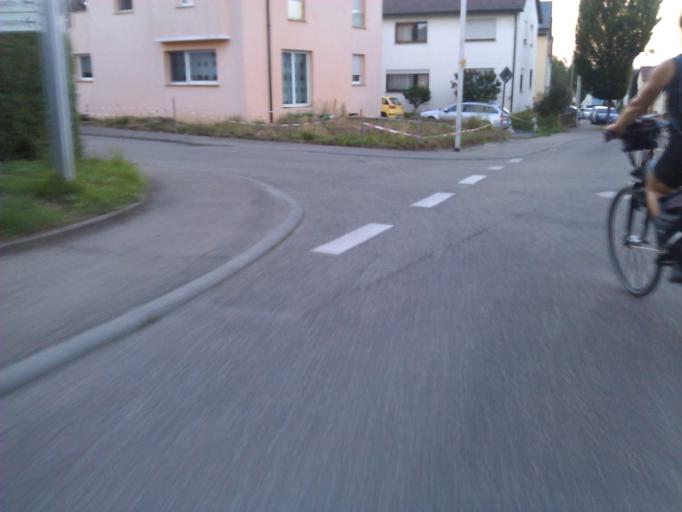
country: DE
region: Baden-Wuerttemberg
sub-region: Regierungsbezirk Stuttgart
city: Leingarten
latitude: 49.1400
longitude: 9.1277
